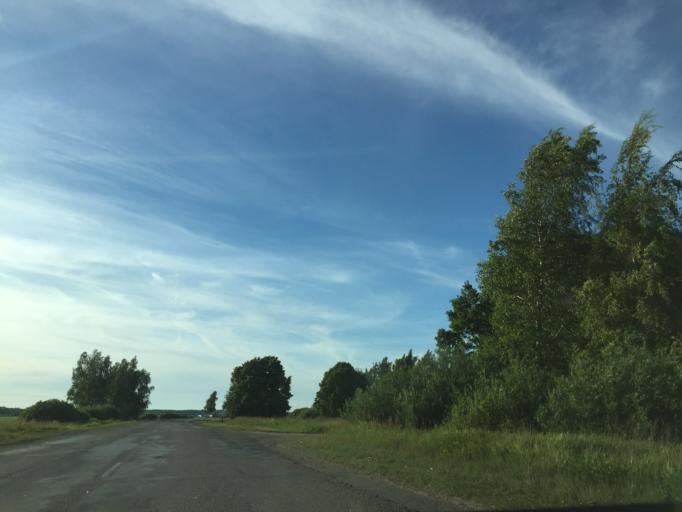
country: LV
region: Ventspils
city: Ventspils
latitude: 57.3471
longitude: 21.5673
